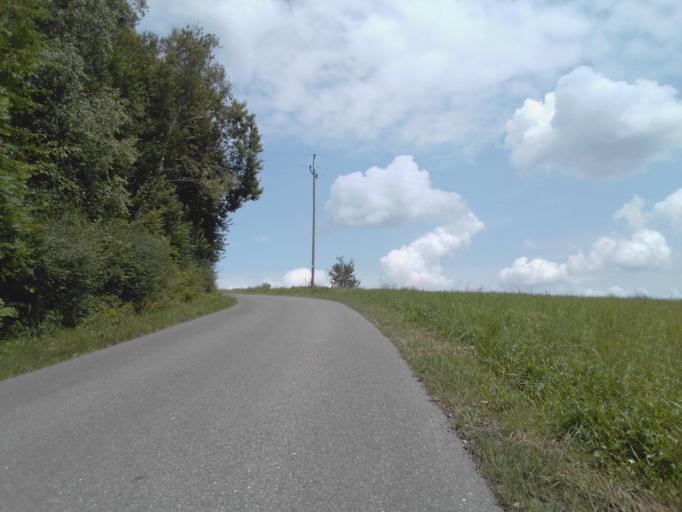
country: PL
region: Subcarpathian Voivodeship
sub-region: Powiat strzyzowski
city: Frysztak
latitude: 49.8200
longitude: 21.5943
